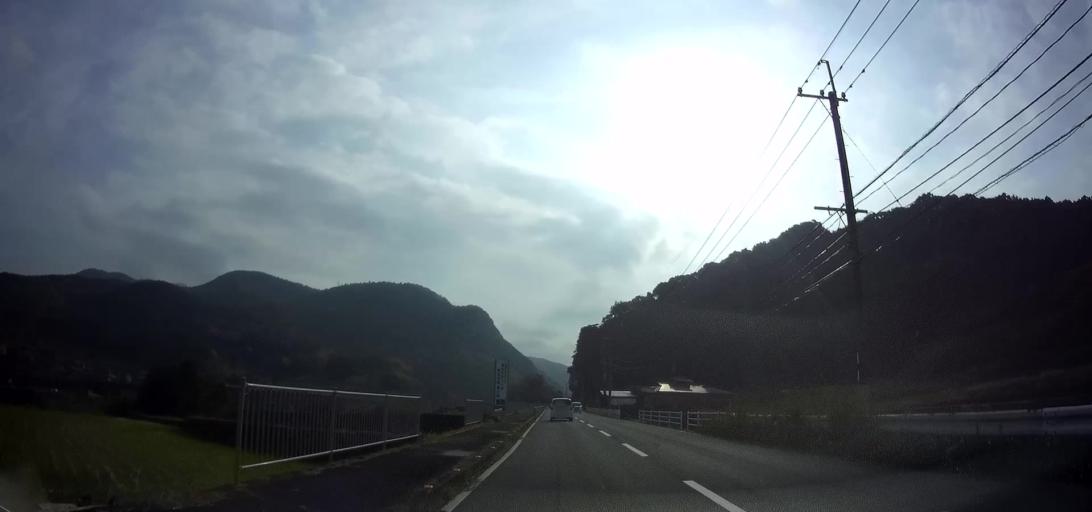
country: JP
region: Nagasaki
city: Shimabara
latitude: 32.7805
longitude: 130.2076
